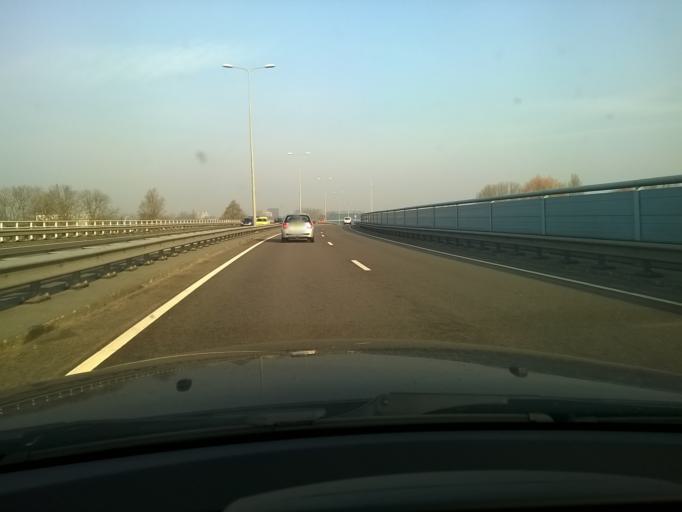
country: NL
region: Groningen
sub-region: Gemeente Groningen
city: Groningen
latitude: 53.2124
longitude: 6.5426
